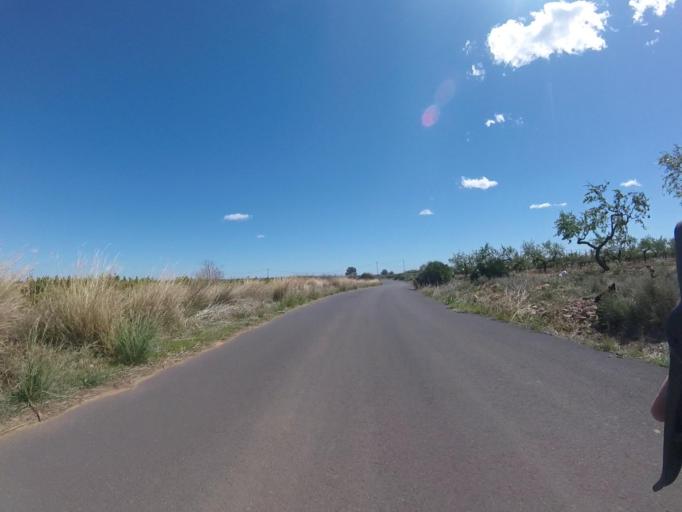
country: ES
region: Valencia
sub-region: Provincia de Castello
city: Orpesa/Oropesa del Mar
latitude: 40.1663
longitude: 0.1546
